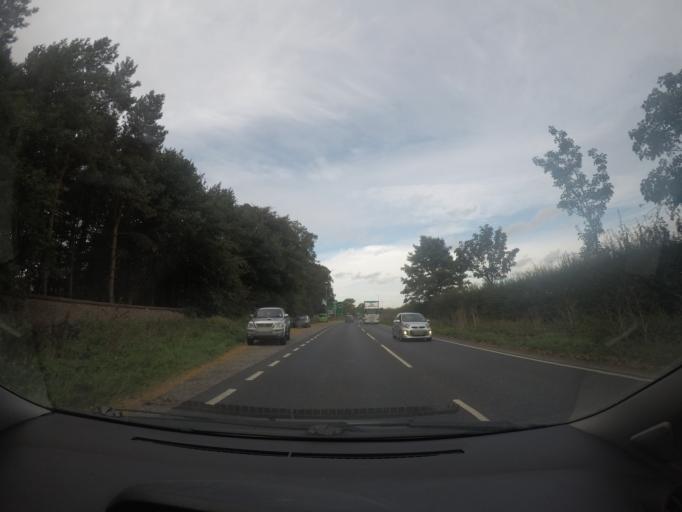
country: GB
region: England
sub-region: City of York
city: Fulford
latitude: 53.9208
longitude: -1.0634
